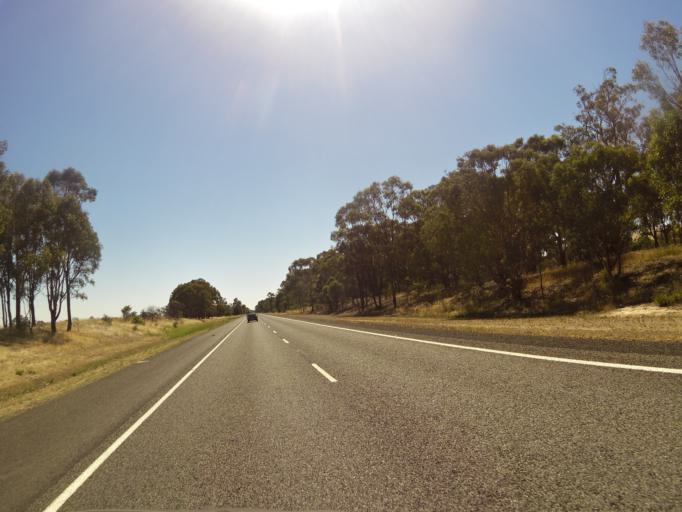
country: AU
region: Victoria
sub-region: Greater Shepparton
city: Shepparton
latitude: -36.8716
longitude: 145.2852
